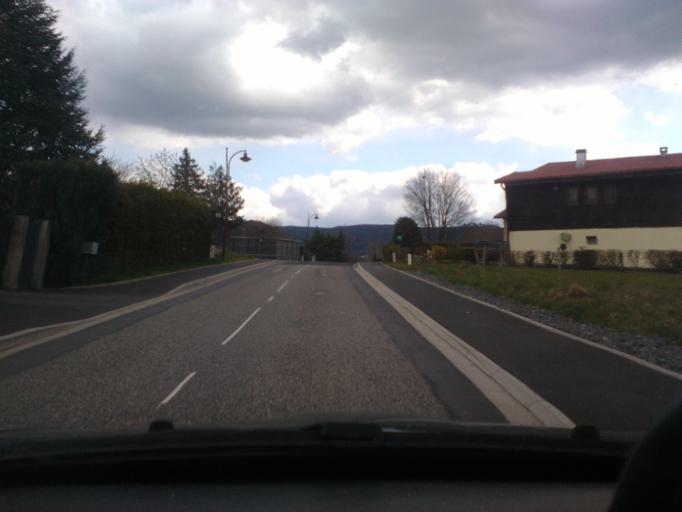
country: FR
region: Lorraine
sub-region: Departement des Vosges
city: Etival-Clairefontaine
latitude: 48.3258
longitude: 6.8270
